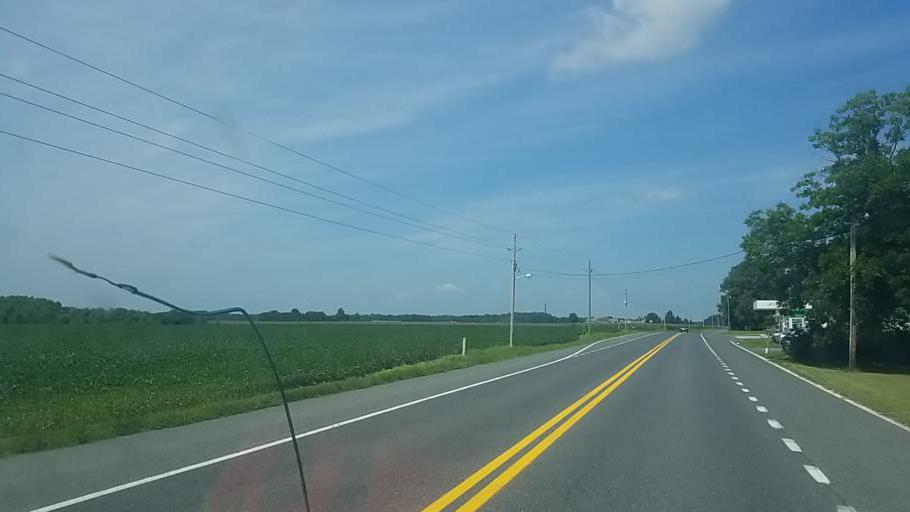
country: US
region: Delaware
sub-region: Sussex County
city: Bridgeville
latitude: 38.8260
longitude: -75.6519
